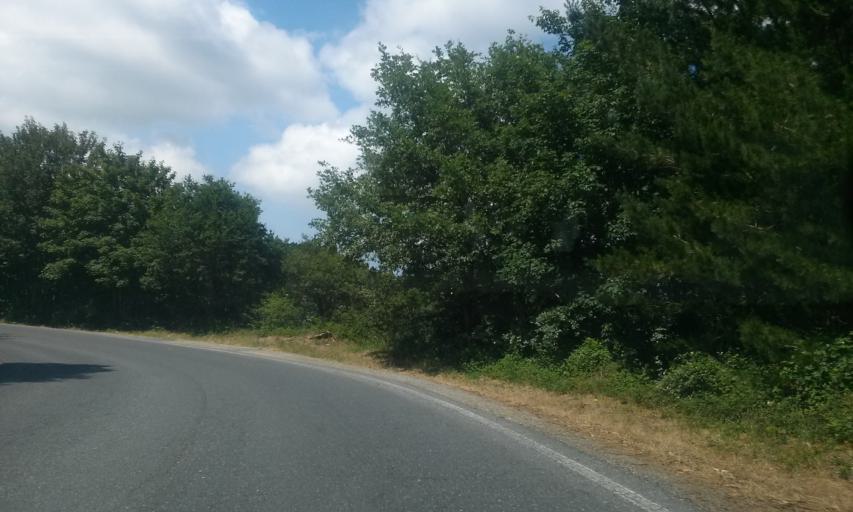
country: ES
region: Galicia
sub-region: Provincia de Lugo
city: Guitiriz
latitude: 43.1737
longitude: -7.8312
